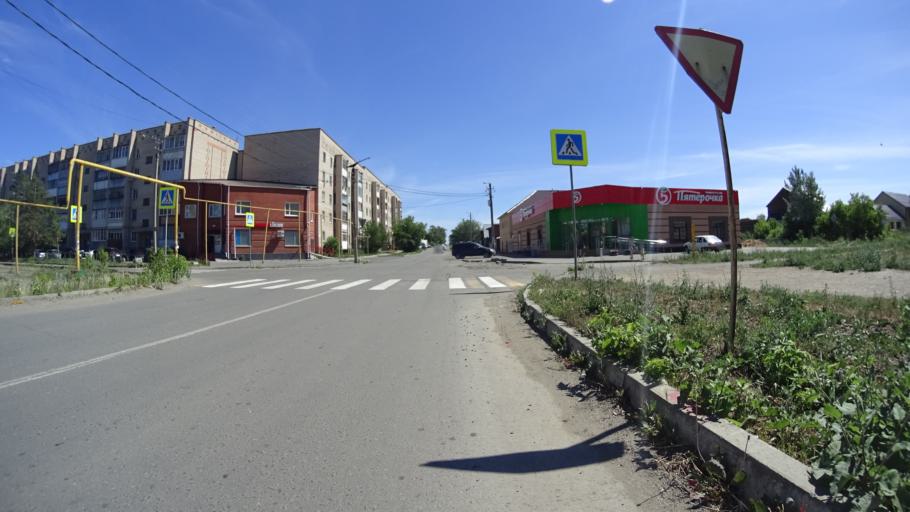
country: RU
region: Chelyabinsk
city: Troitsk
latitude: 54.0914
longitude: 61.5503
